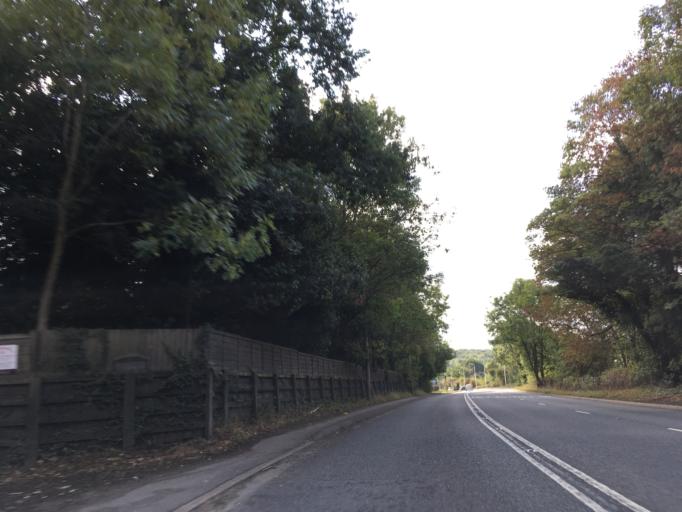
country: GB
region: England
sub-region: West Berkshire
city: Greenham
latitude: 51.3785
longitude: -1.3187
